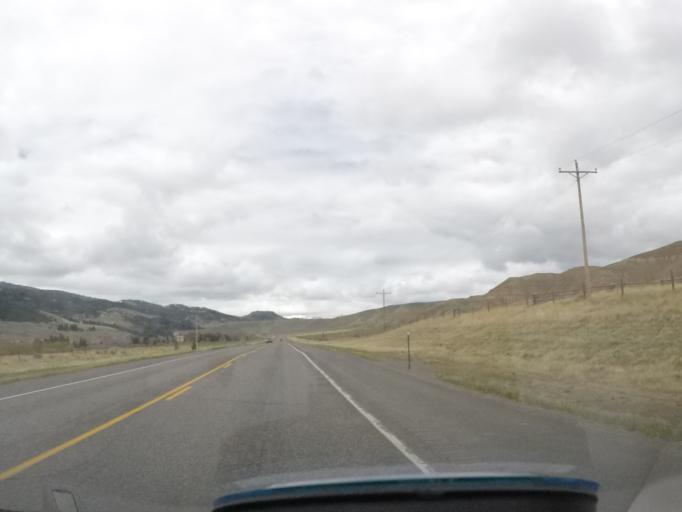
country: US
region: Wyoming
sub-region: Sublette County
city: Pinedale
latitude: 43.5727
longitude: -109.7244
